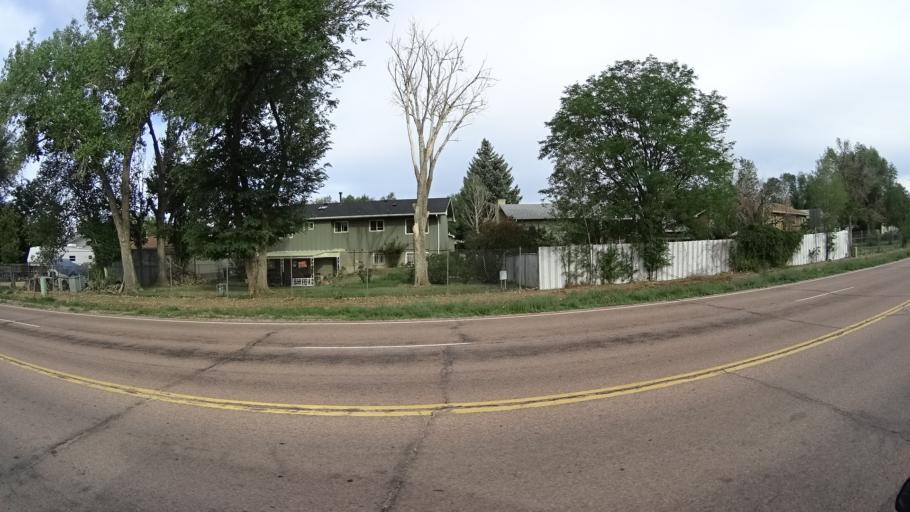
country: US
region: Colorado
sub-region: El Paso County
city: Security-Widefield
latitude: 38.7244
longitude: -104.6990
